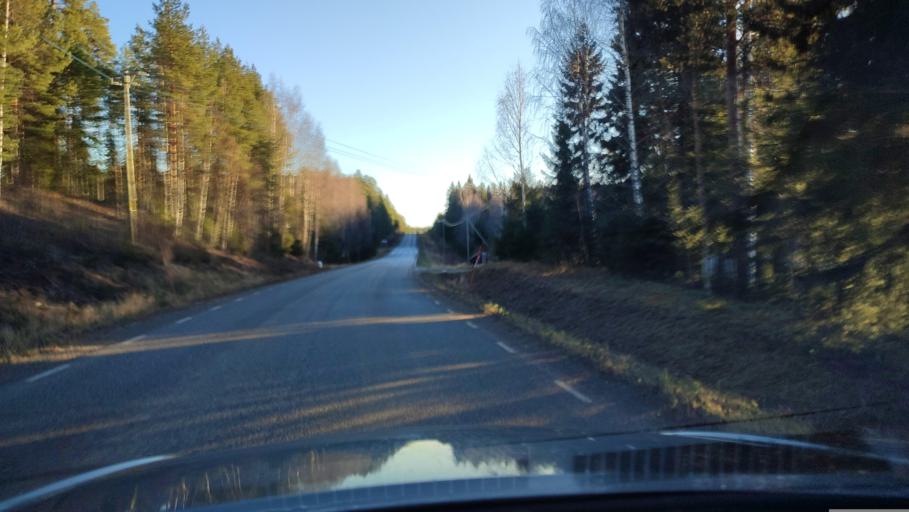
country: SE
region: Vaesterbotten
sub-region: Skelleftea Kommun
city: Viken
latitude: 64.6961
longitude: 20.9234
